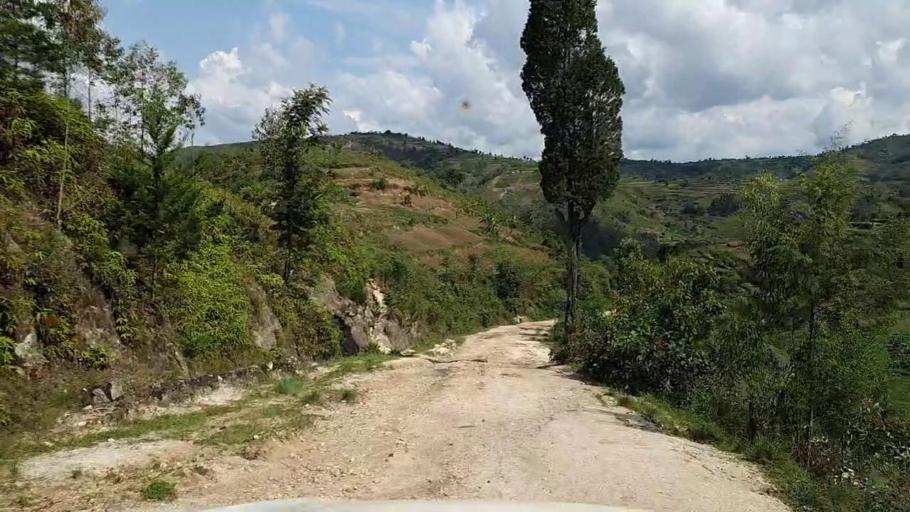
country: RW
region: Southern Province
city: Gikongoro
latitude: -2.3986
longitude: 29.5603
